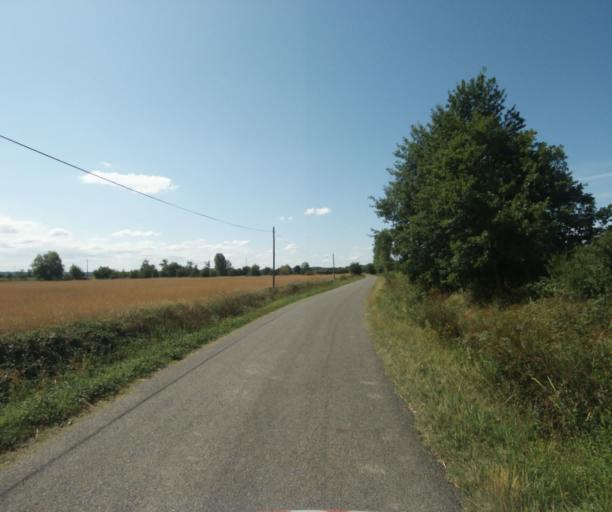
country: FR
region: Midi-Pyrenees
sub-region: Departement de la Haute-Garonne
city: Revel
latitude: 43.4744
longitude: 1.9815
